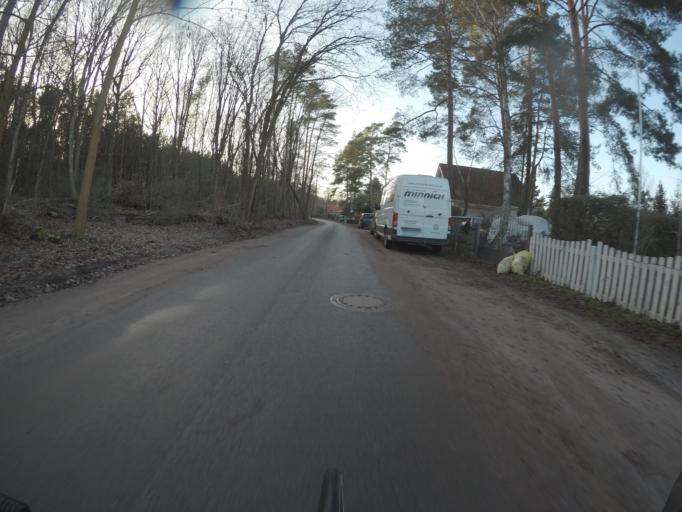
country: DE
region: Brandenburg
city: Birkenwerder
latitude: 52.6852
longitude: 13.3160
